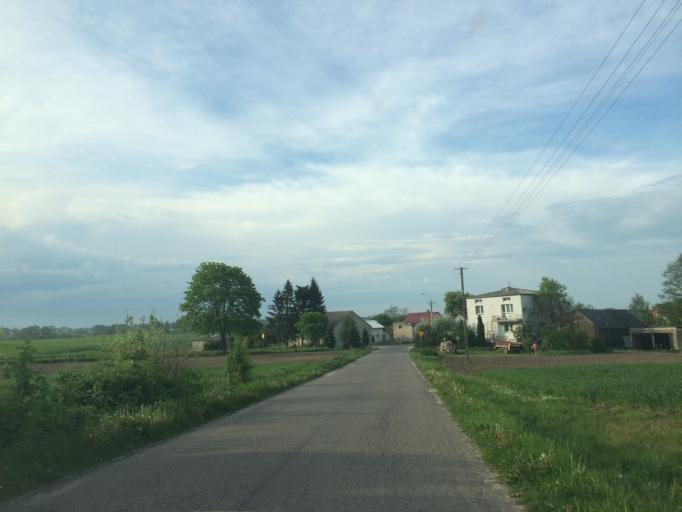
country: PL
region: Kujawsko-Pomorskie
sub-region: Powiat brodnicki
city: Brzozie
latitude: 53.3531
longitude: 19.6015
